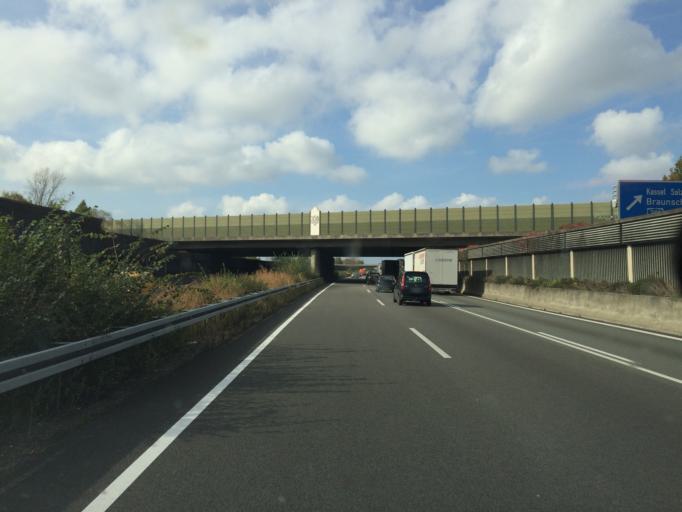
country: DE
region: Lower Saxony
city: Braunschweig
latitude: 52.3143
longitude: 10.5193
